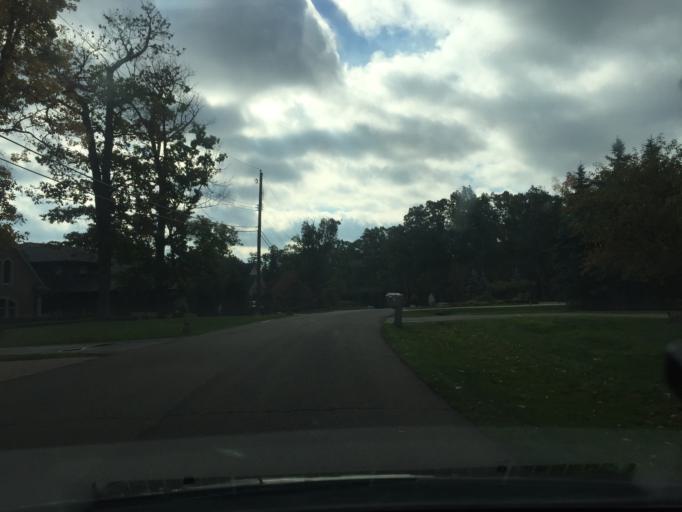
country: US
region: Michigan
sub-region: Oakland County
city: Sylvan Lake
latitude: 42.5929
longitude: -83.3187
